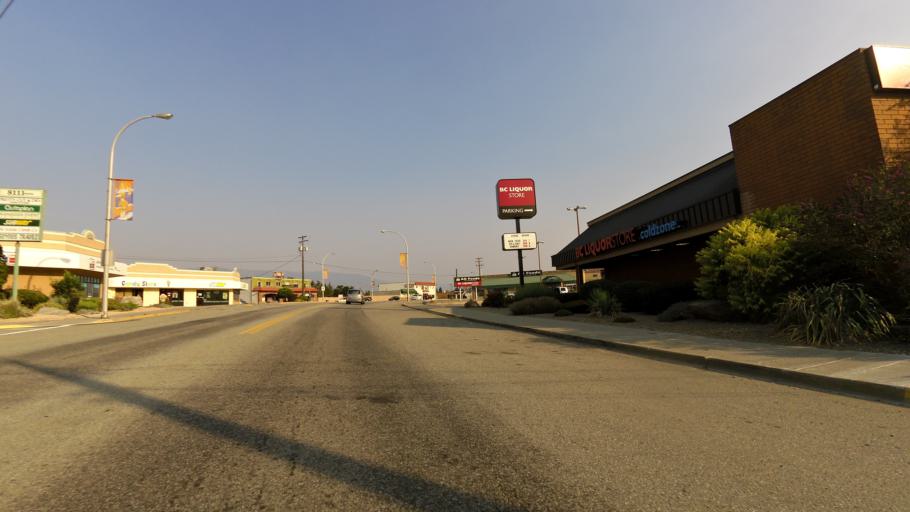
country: CA
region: British Columbia
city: Osoyoos
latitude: 49.0298
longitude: -119.4621
